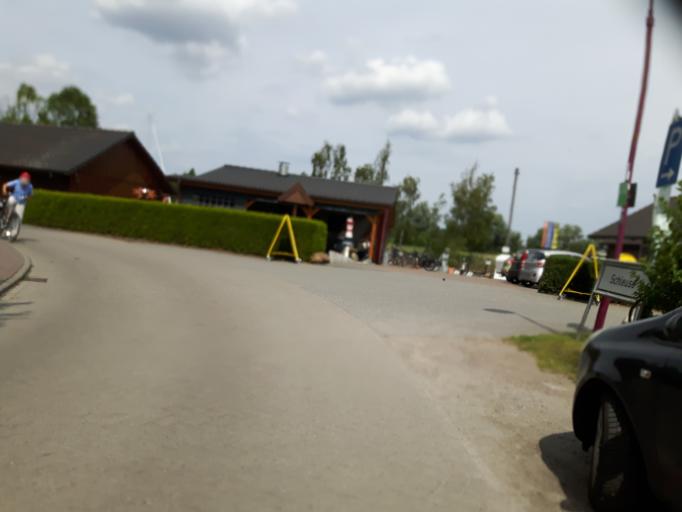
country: DE
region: Lower Saxony
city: Varel
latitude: 53.4076
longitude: 8.1811
